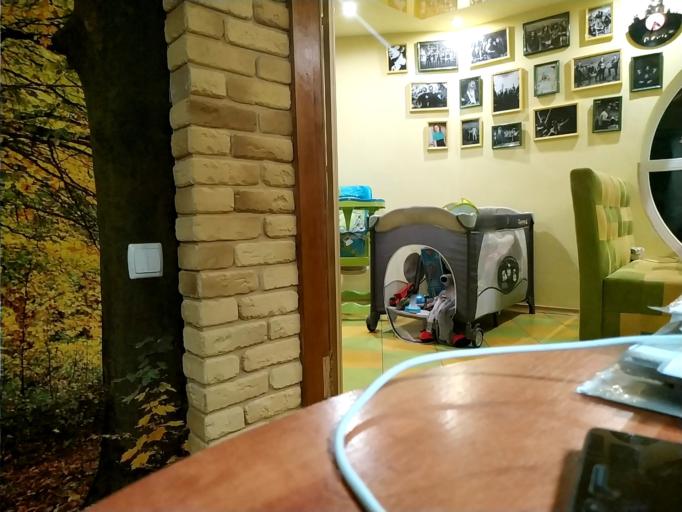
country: RU
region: Smolensk
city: Vyaz'ma
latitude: 55.2258
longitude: 34.1716
